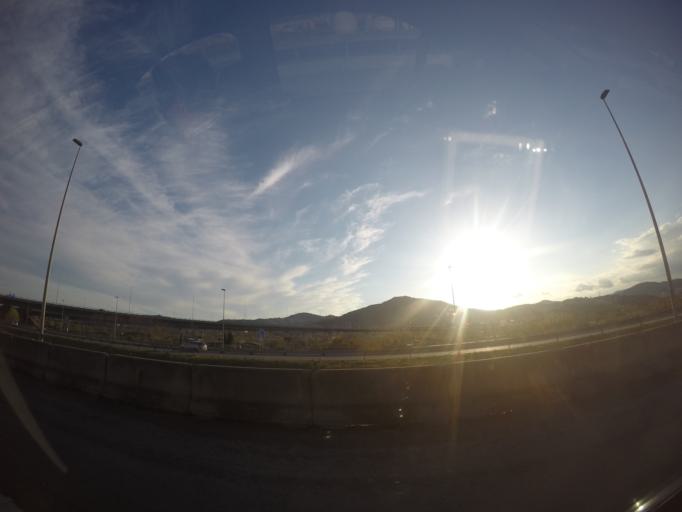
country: ES
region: Catalonia
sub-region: Provincia de Barcelona
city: Sant Feliu de Llobregat
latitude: 41.3829
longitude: 2.0289
